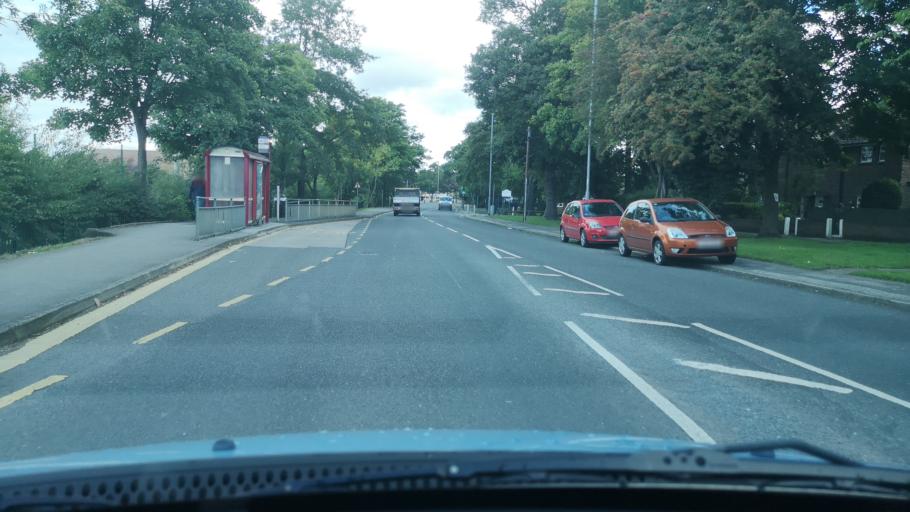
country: GB
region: England
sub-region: City and Borough of Wakefield
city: Crigglestone
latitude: 53.6465
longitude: -1.5005
